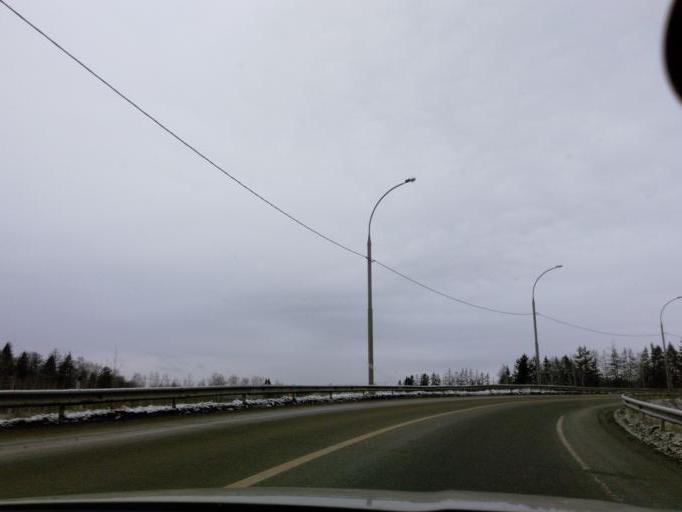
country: RU
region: Moskovskaya
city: Novopodrezkovo
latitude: 55.9656
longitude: 37.3250
